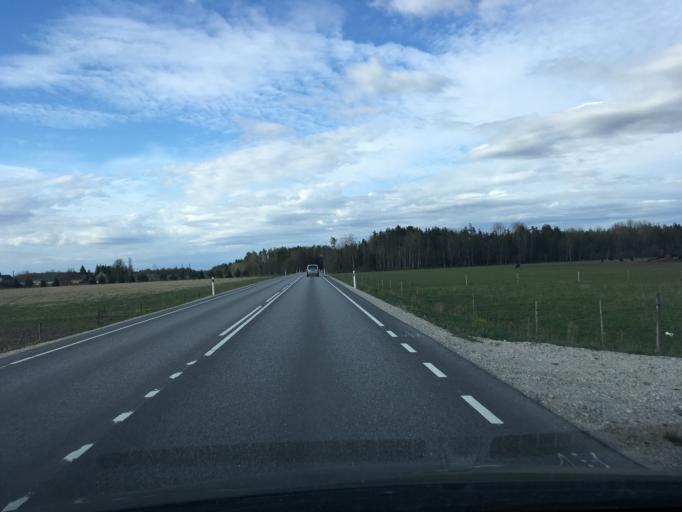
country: EE
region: Raplamaa
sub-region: Maerjamaa vald
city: Marjamaa
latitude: 58.9177
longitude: 24.2929
